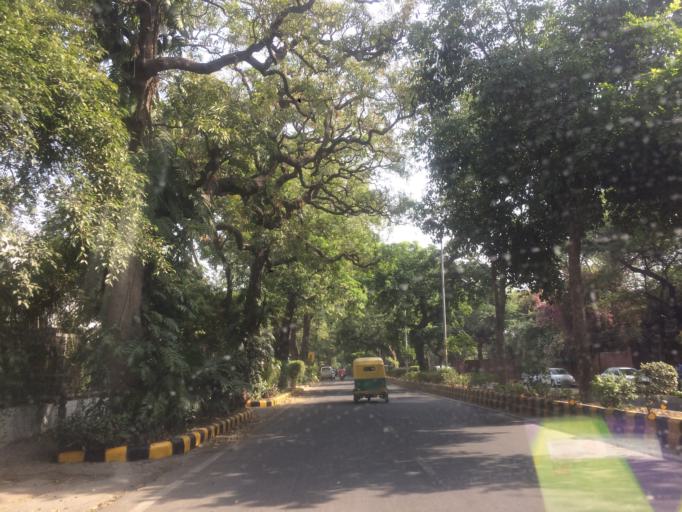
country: IN
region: NCT
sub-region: New Delhi
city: New Delhi
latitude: 28.5965
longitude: 77.2322
